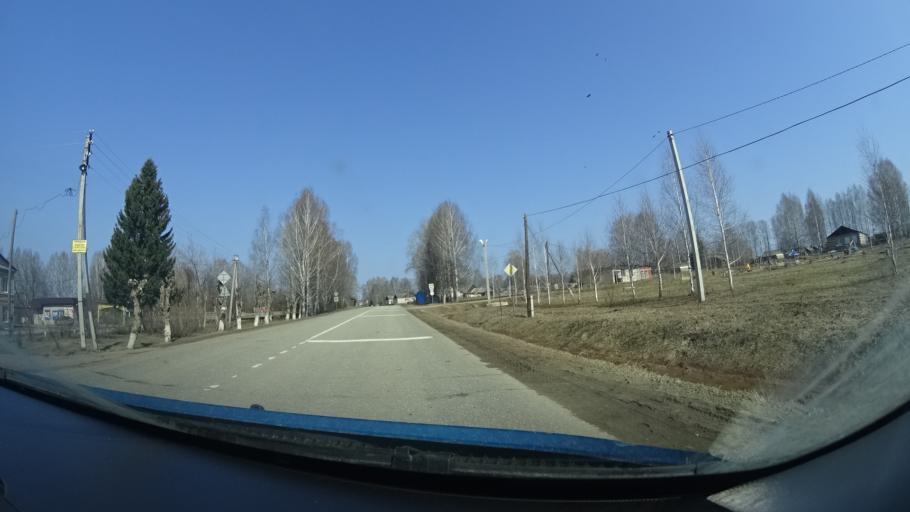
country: RU
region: Perm
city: Osa
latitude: 57.3697
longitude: 55.6076
